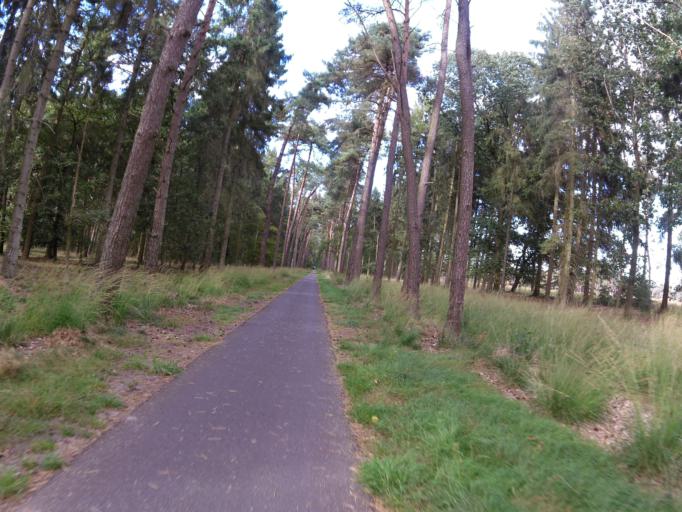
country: NL
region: North Brabant
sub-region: Gemeente Valkenswaard
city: Valkenswaard
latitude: 51.3549
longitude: 5.5136
